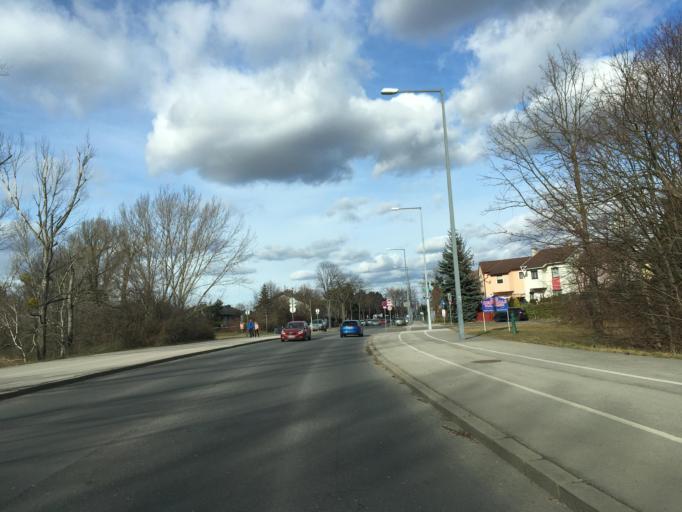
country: AT
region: Lower Austria
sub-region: Politischer Bezirk Wien-Umgebung
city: Schwechat
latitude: 48.2057
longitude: 16.4762
